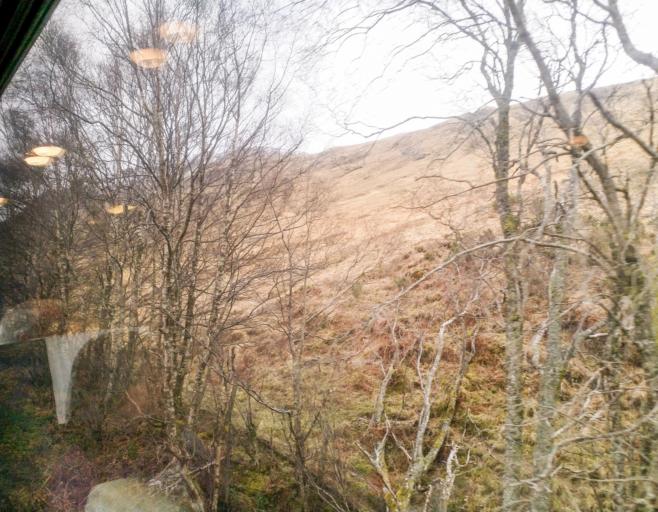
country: GB
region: Scotland
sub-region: Highland
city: Spean Bridge
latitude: 56.8143
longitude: -4.7152
